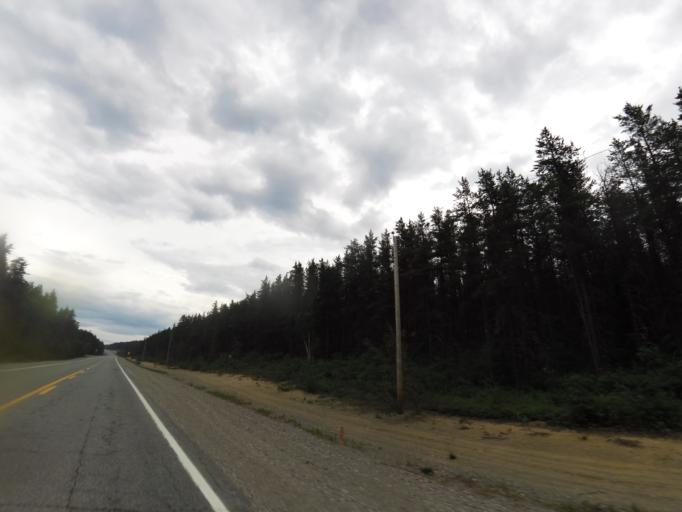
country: CA
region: Quebec
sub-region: Abitibi-Temiscamingue
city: Amos
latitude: 48.8224
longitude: -77.9294
